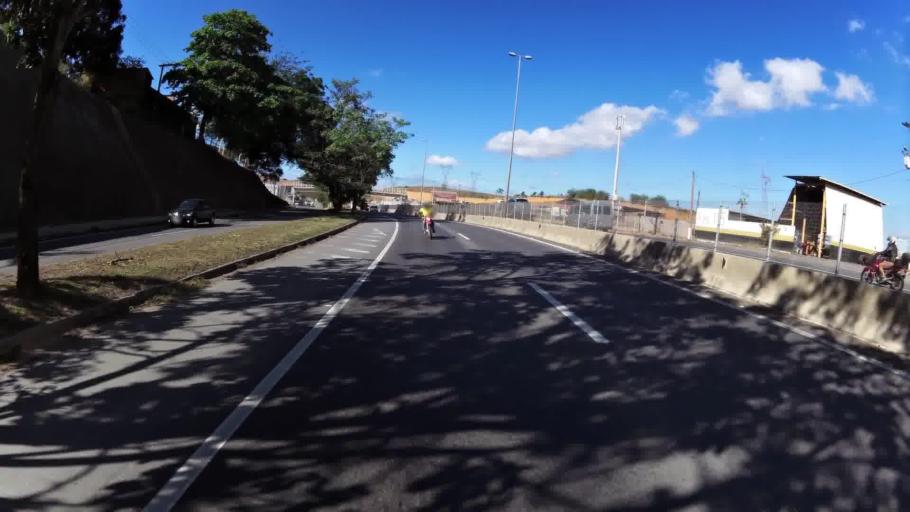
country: BR
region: Espirito Santo
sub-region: Viana
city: Viana
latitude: -20.3625
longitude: -40.4368
